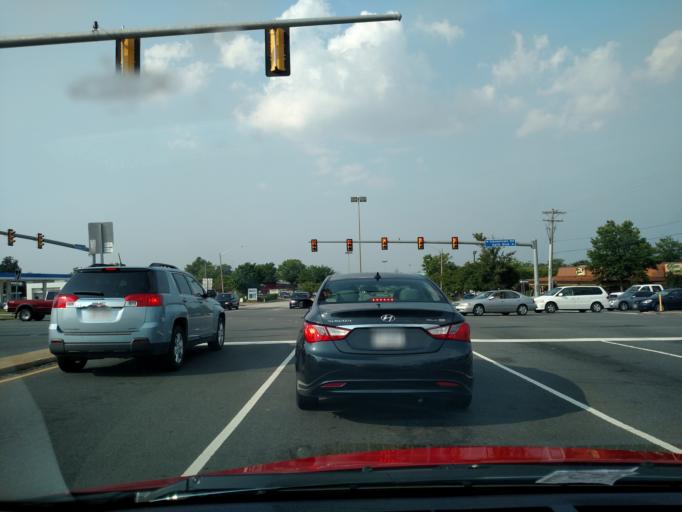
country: US
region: Virginia
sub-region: Prince William County
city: Potomac Mills
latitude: 38.6380
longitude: -77.2981
